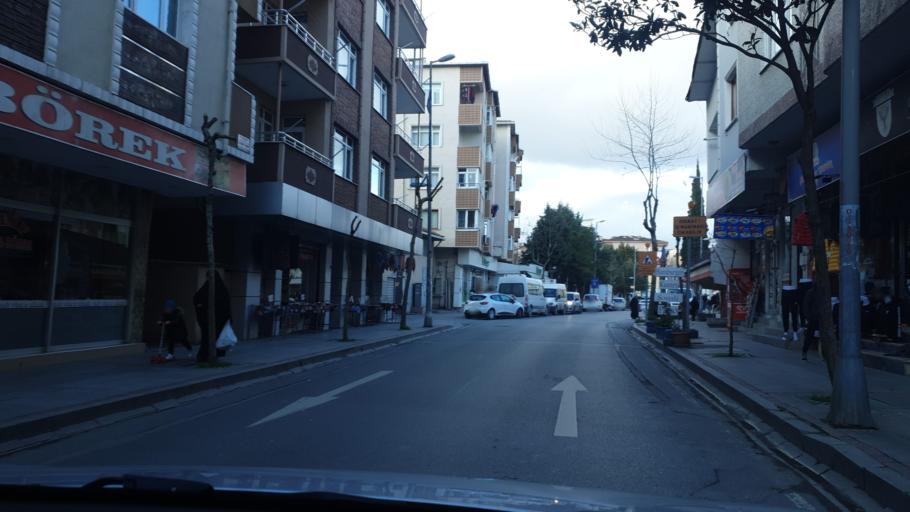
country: TR
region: Istanbul
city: Pendik
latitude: 40.8771
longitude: 29.2735
